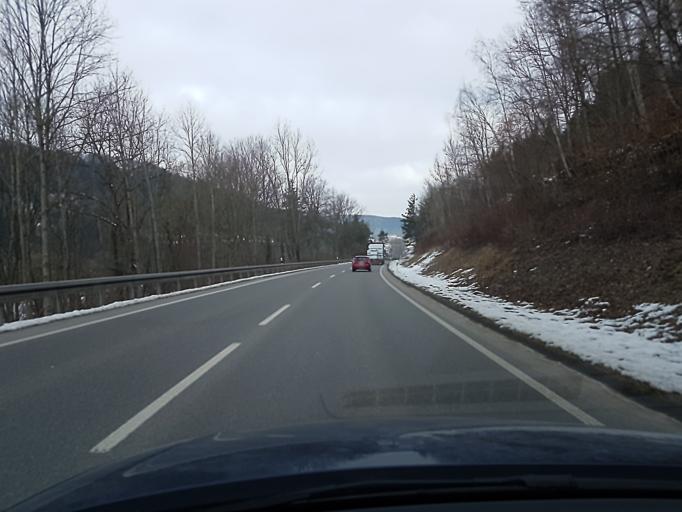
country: DE
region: Baden-Wuerttemberg
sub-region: Freiburg Region
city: Sulz am Neckar
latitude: 48.4016
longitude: 8.6438
